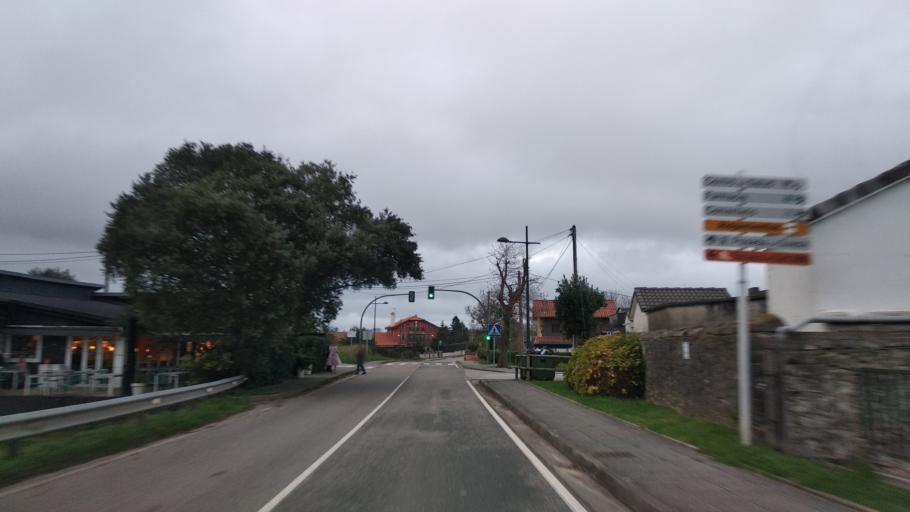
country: ES
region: Cantabria
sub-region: Provincia de Cantabria
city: Entrambasaguas
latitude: 43.4400
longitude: -3.7153
